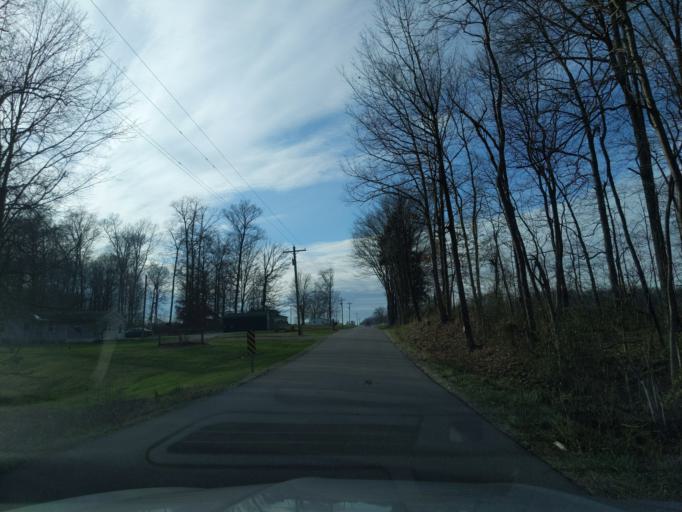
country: US
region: Indiana
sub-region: Decatur County
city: Westport
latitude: 39.1905
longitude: -85.5215
